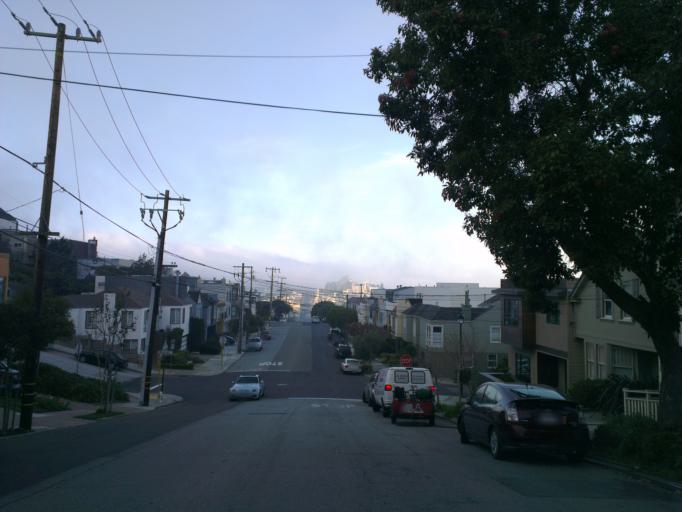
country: US
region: California
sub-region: San Francisco County
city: San Francisco
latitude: 37.7451
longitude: -122.4357
